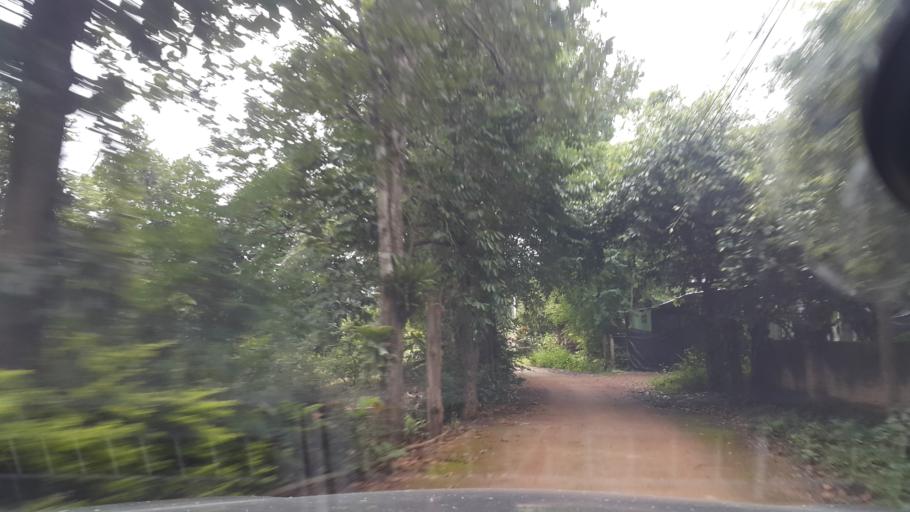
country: TH
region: Chiang Mai
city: San Sai
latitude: 18.9913
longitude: 99.1307
